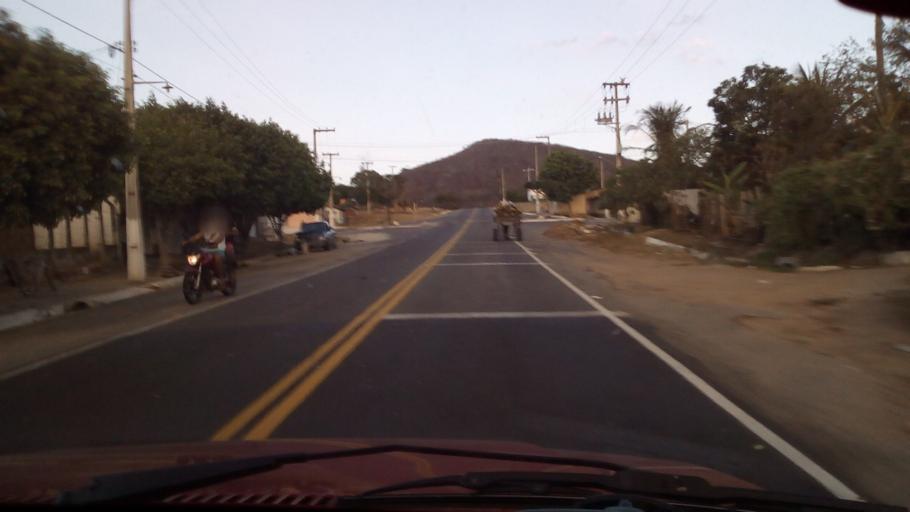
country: BR
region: Paraiba
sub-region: Belem
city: Belem
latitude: -6.7206
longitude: -35.5423
